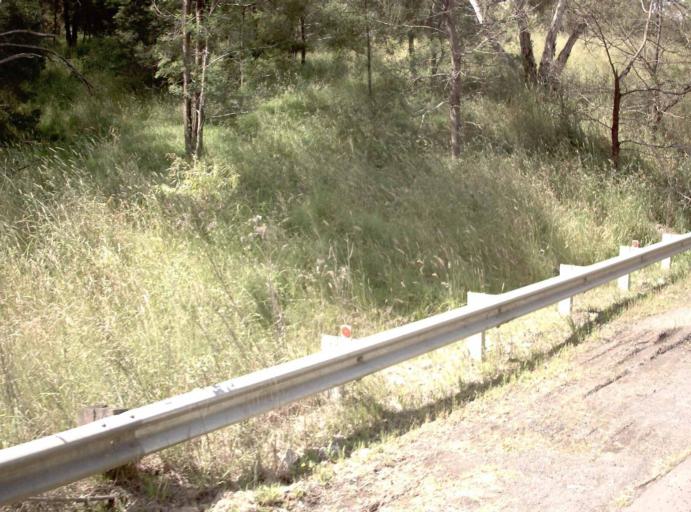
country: AU
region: Victoria
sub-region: Latrobe
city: Morwell
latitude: -38.1707
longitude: 146.3511
